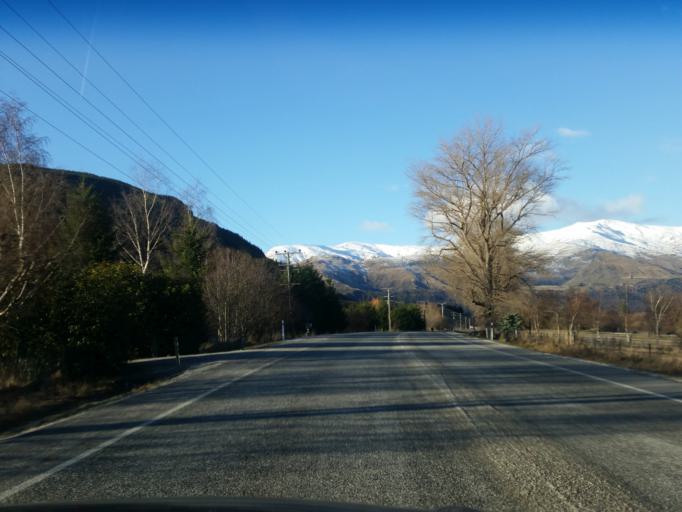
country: NZ
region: Otago
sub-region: Queenstown-Lakes District
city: Arrowtown
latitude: -44.9465
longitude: 168.7862
